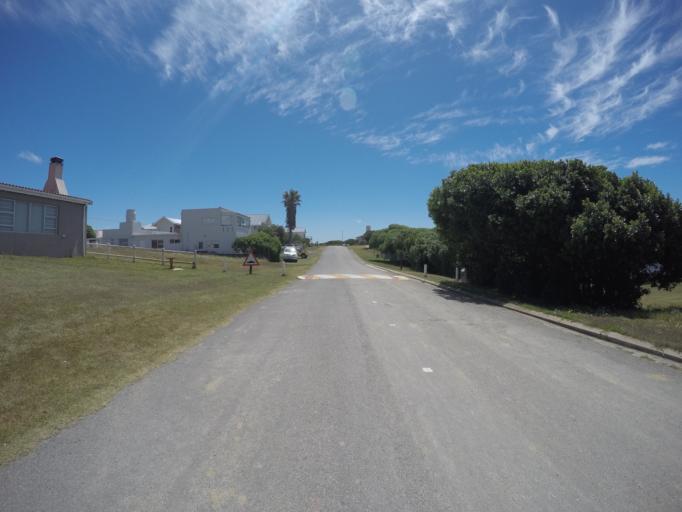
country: ZA
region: Western Cape
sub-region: Eden District Municipality
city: Riversdale
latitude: -34.4211
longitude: 20.8546
